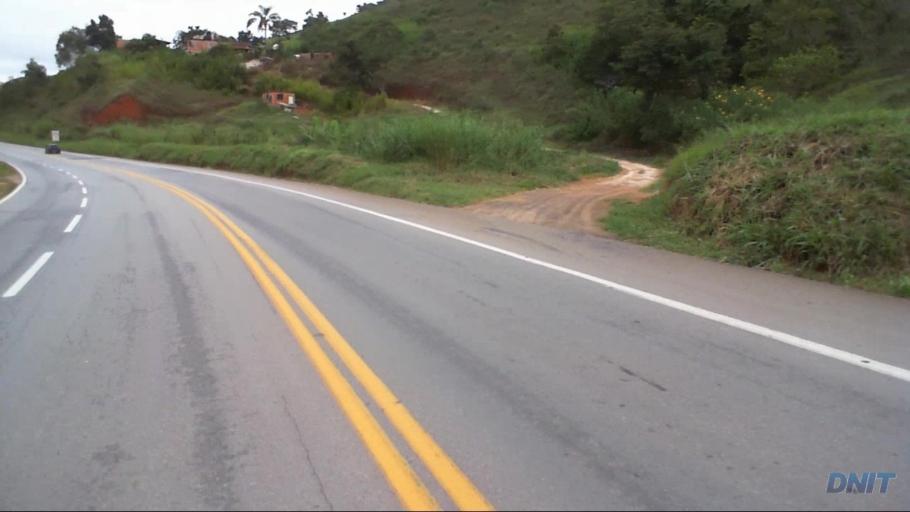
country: BR
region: Minas Gerais
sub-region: Joao Monlevade
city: Joao Monlevade
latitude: -19.8495
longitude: -43.1601
